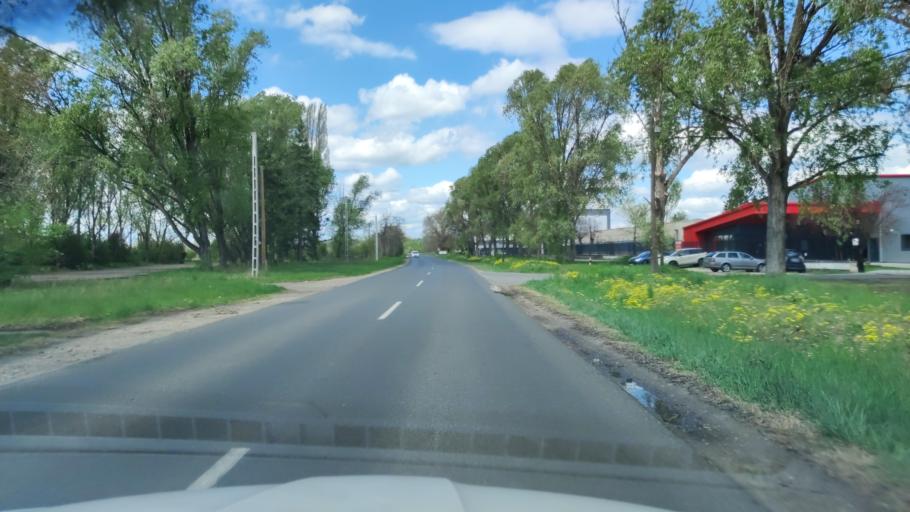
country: HU
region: Pest
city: Cegled
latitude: 47.1626
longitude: 19.8406
